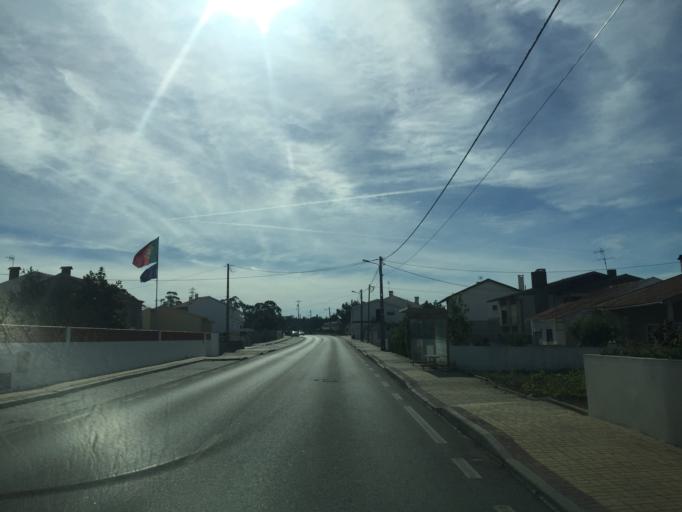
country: PT
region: Coimbra
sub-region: Figueira da Foz
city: Lavos
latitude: 40.0874
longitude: -8.8265
